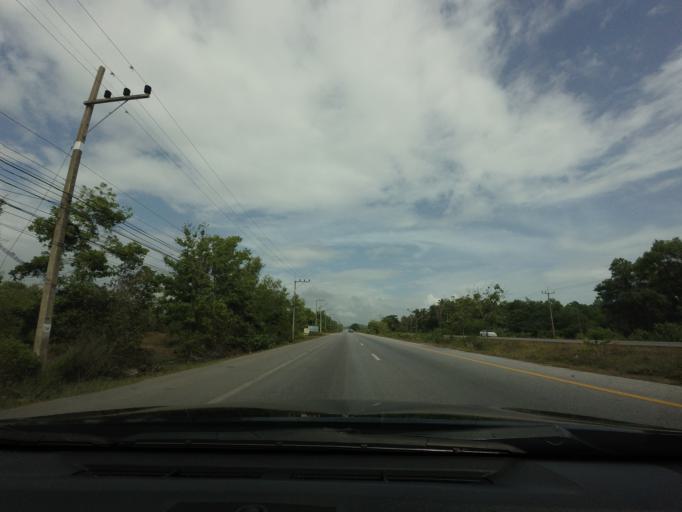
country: TH
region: Songkhla
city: Thepha
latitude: 6.8975
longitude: 100.9186
